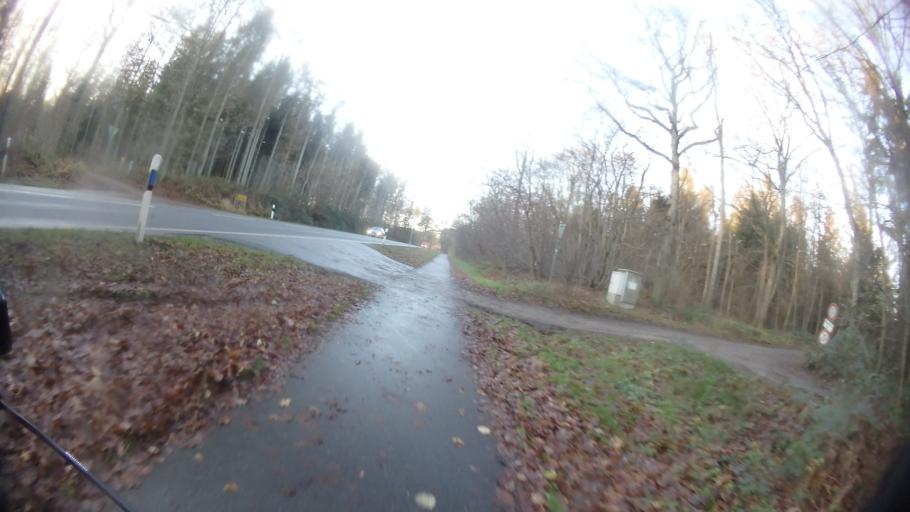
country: DE
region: Schleswig-Holstein
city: Ratekau
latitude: 53.9992
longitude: 10.7026
